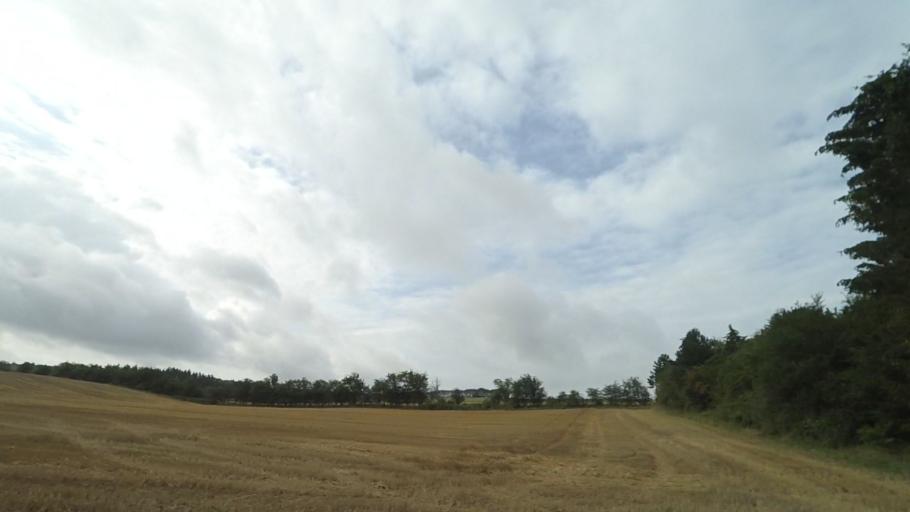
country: DK
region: Central Jutland
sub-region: Syddjurs Kommune
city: Ronde
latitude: 56.3375
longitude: 10.4735
